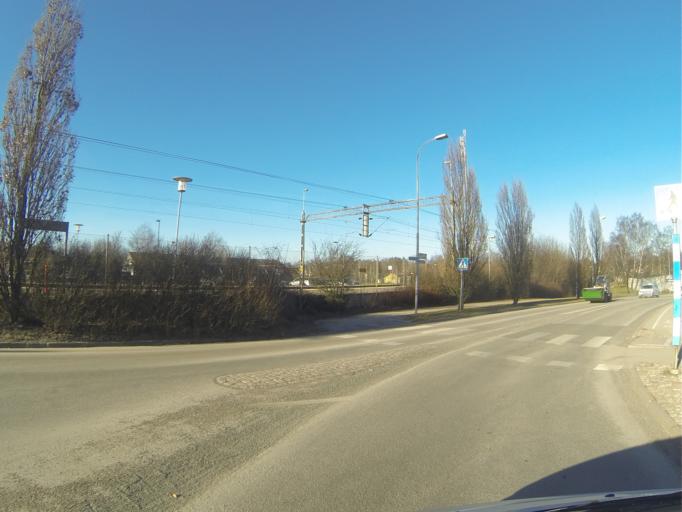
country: SE
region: Skane
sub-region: Hoors Kommun
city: Hoeoer
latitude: 55.9383
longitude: 13.5455
